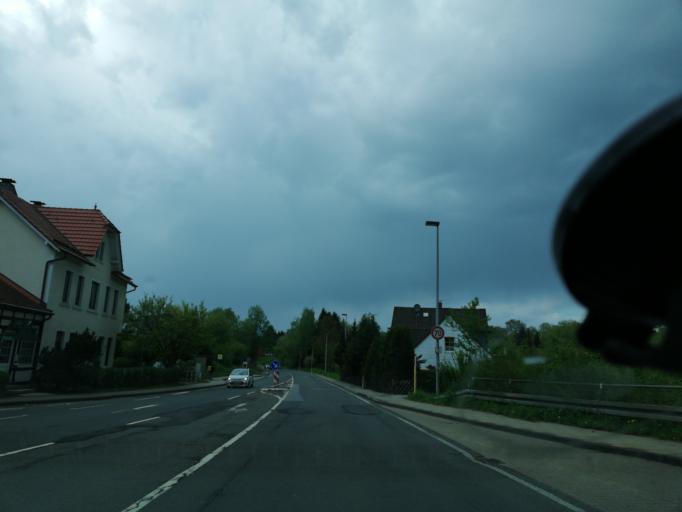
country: DE
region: North Rhine-Westphalia
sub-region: Regierungsbezirk Arnsberg
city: Schwelm
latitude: 51.3234
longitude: 7.2879
